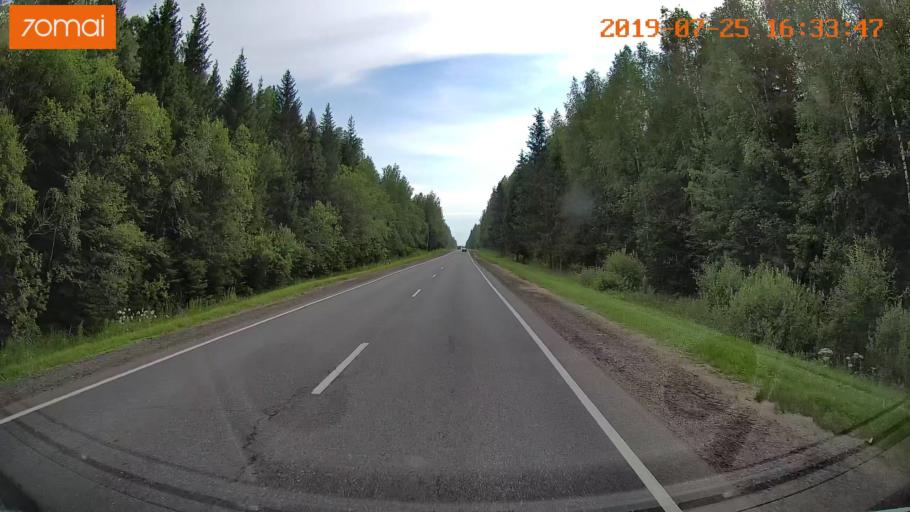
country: RU
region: Ivanovo
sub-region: Privolzhskiy Rayon
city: Ples
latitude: 57.4235
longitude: 41.4497
